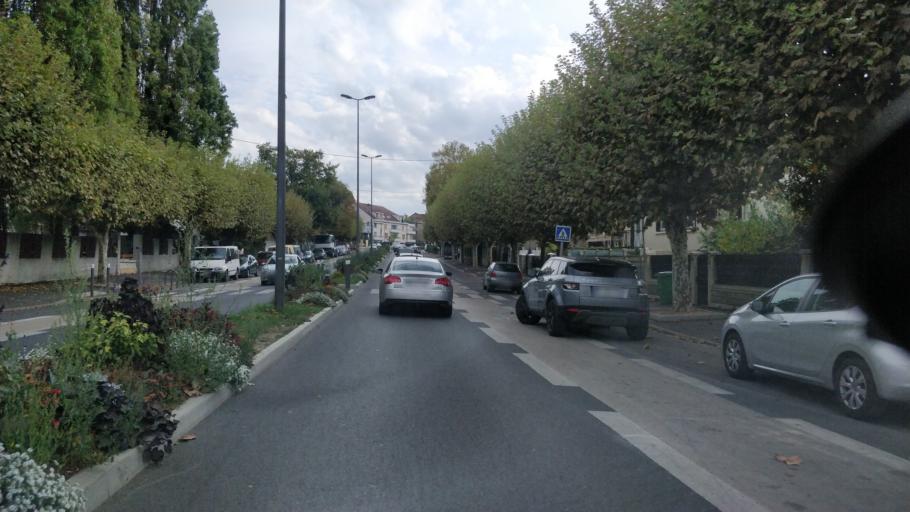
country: FR
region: Ile-de-France
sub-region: Departement de Seine-Saint-Denis
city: Clichy-sous-Bois
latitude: 48.9006
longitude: 2.5467
